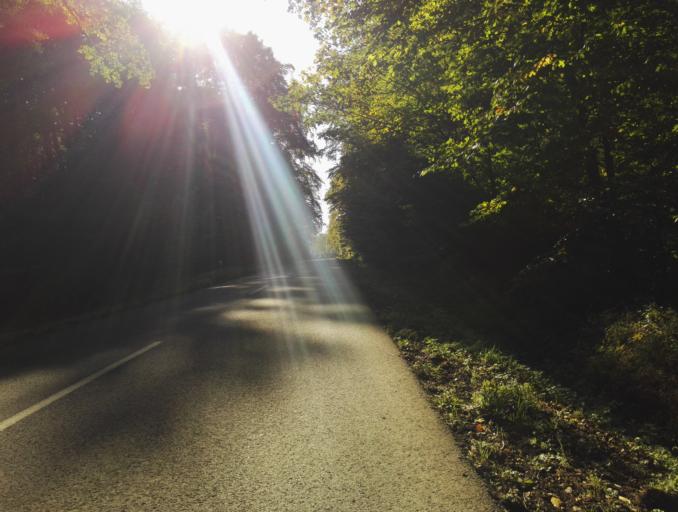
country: DE
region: Lower Saxony
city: Holle
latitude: 52.1241
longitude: 10.1262
